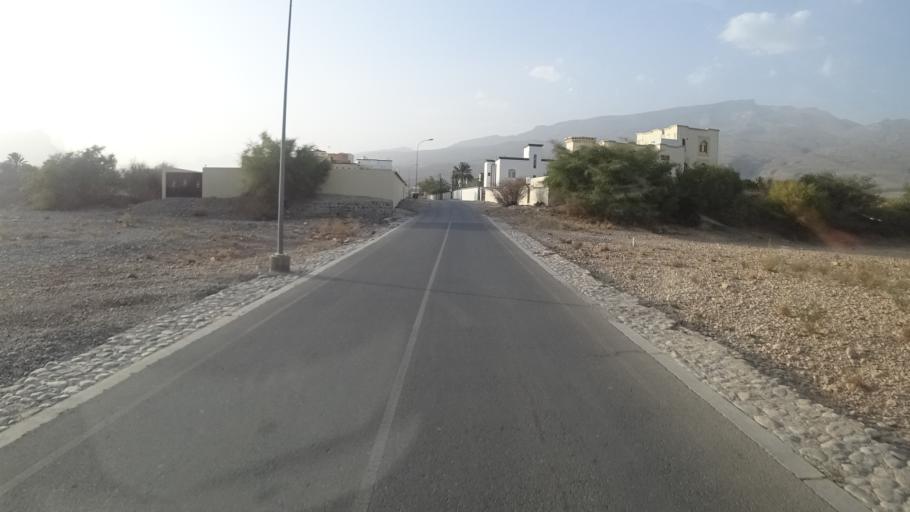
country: OM
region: Muhafazat ad Dakhiliyah
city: Bahla'
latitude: 23.1087
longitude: 57.2946
